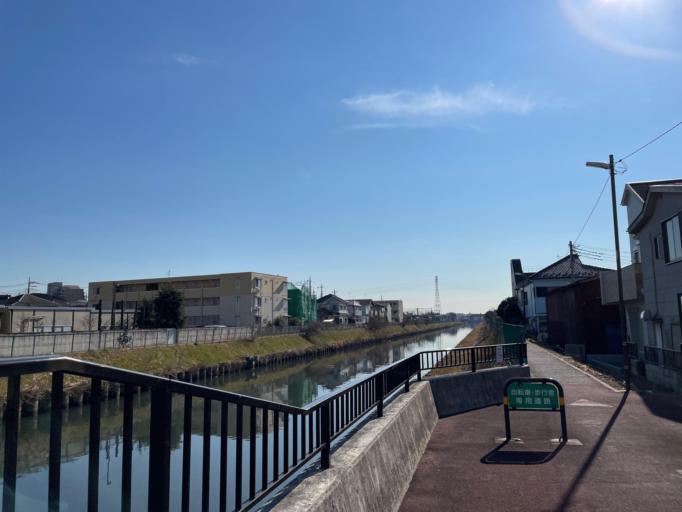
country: JP
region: Saitama
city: Soka
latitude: 35.8133
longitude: 139.7748
